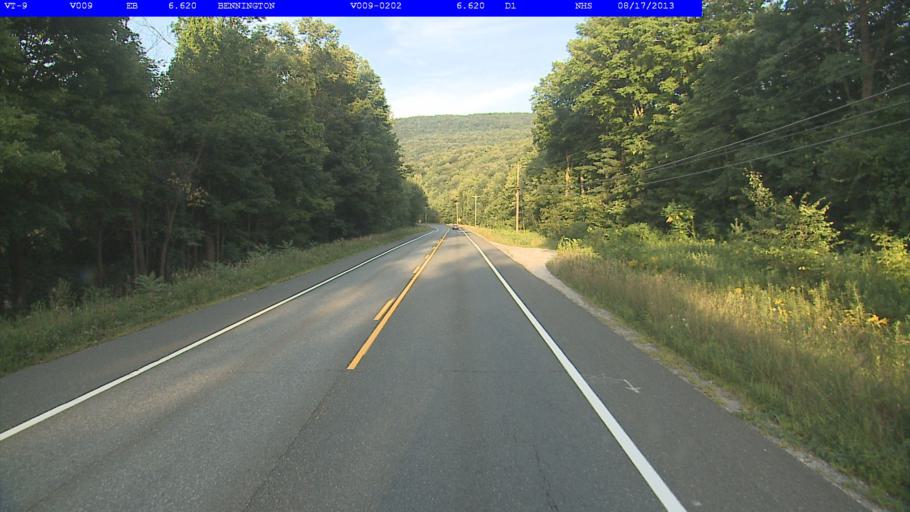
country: US
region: Vermont
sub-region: Bennington County
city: Bennington
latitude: 42.8830
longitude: -73.1547
